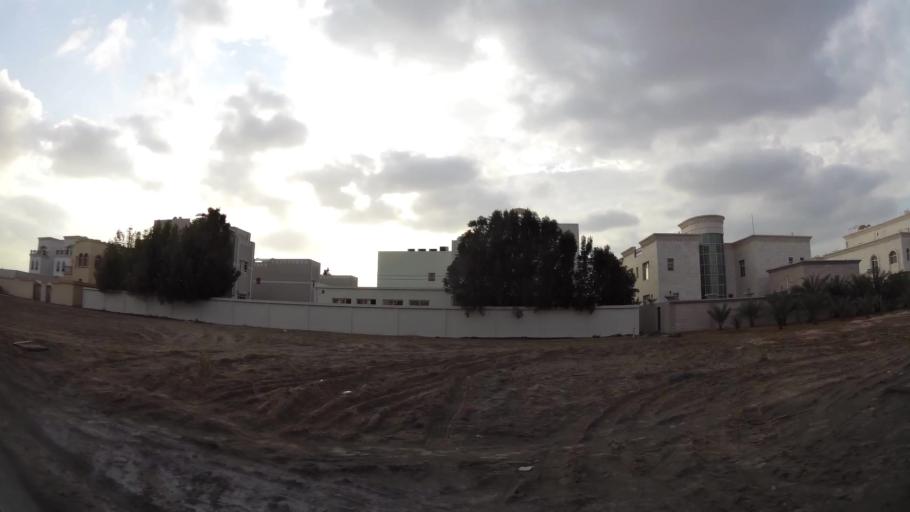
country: AE
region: Abu Dhabi
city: Abu Dhabi
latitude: 24.3561
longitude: 54.5587
